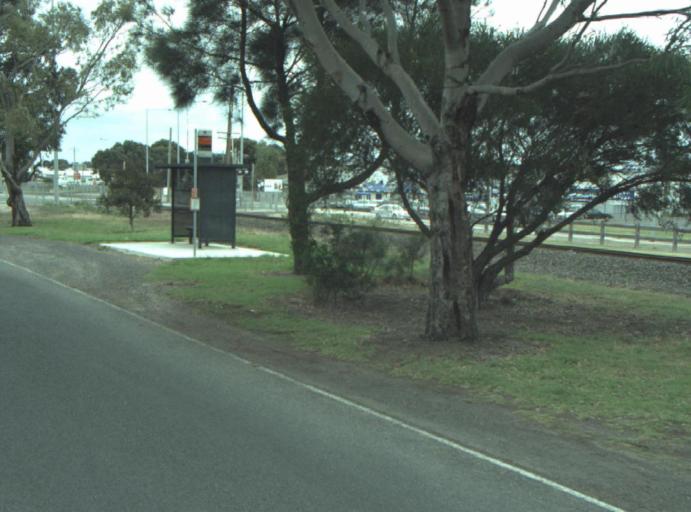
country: AU
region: Victoria
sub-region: Greater Geelong
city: East Geelong
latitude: -38.1653
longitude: 144.3692
